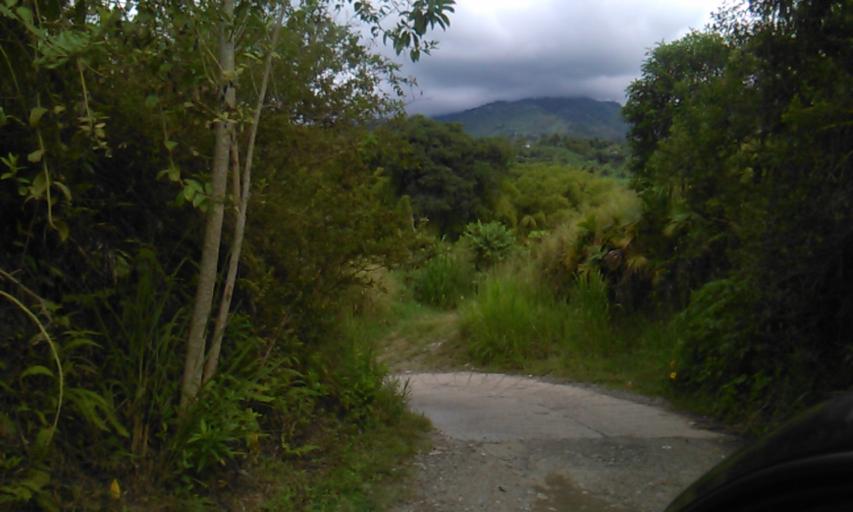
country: CO
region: Quindio
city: Cordoba
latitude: 4.4078
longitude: -75.6890
